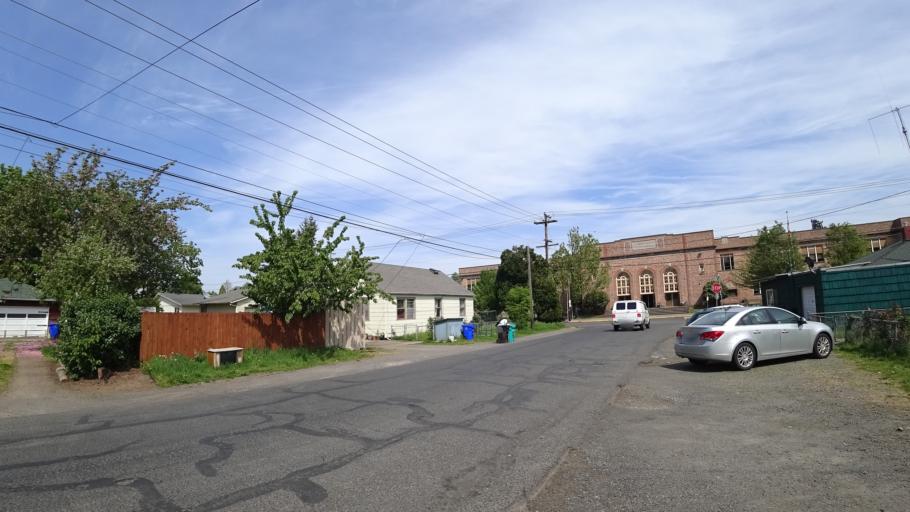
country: US
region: Oregon
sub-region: Multnomah County
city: Lents
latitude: 45.4713
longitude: -122.6027
